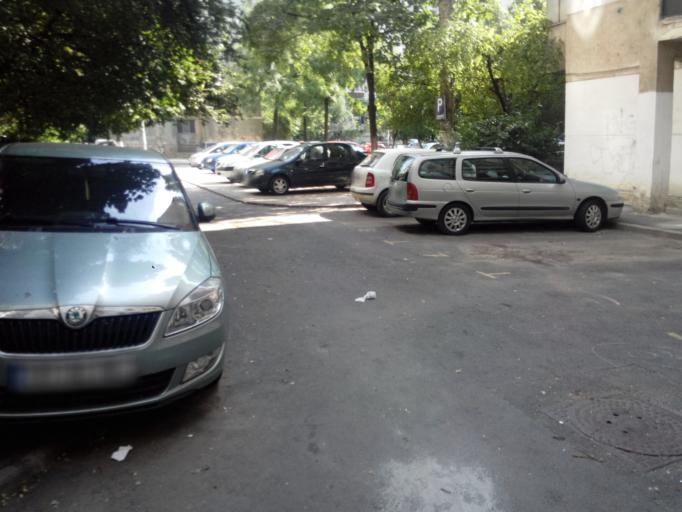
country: RO
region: Ilfov
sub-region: Comuna Chiajna
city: Rosu
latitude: 44.4337
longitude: 26.0276
